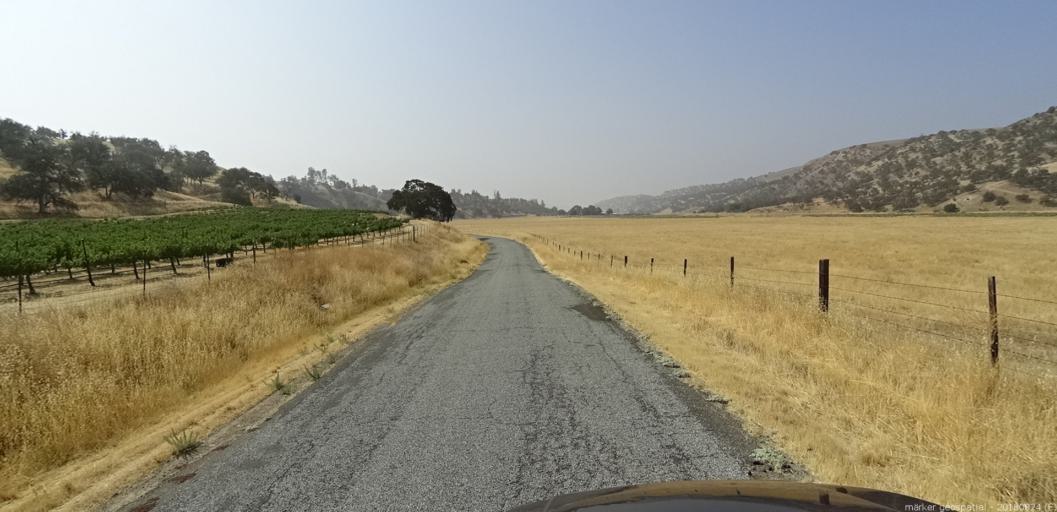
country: US
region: California
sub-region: San Luis Obispo County
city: San Miguel
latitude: 35.8821
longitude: -120.7013
